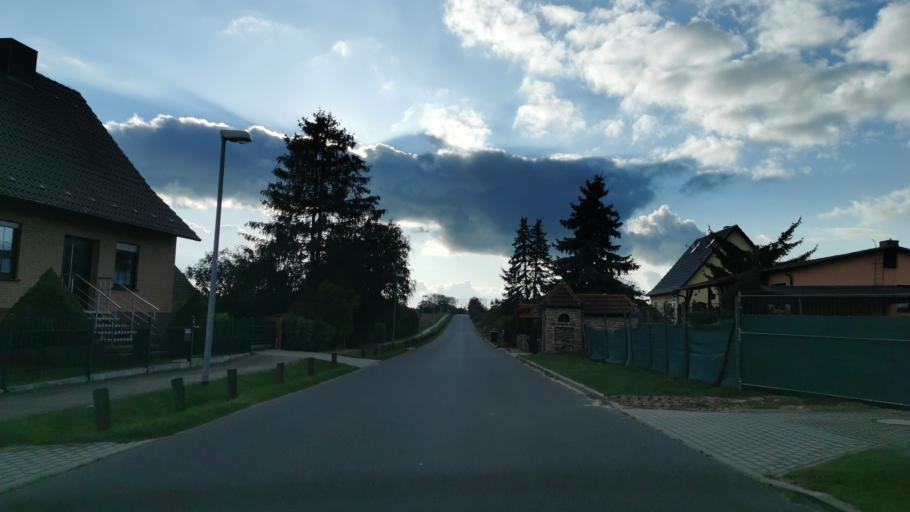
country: DE
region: Brandenburg
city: Werder
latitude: 52.3539
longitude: 12.8915
